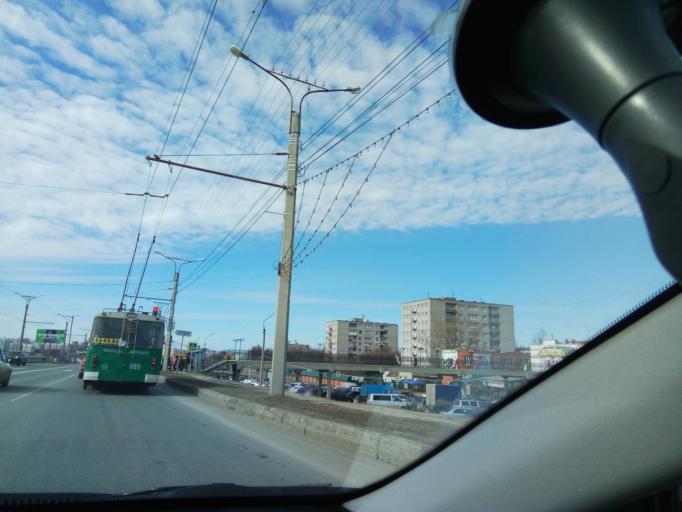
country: RU
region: Chuvashia
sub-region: Cheboksarskiy Rayon
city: Cheboksary
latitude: 56.1222
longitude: 47.2466
